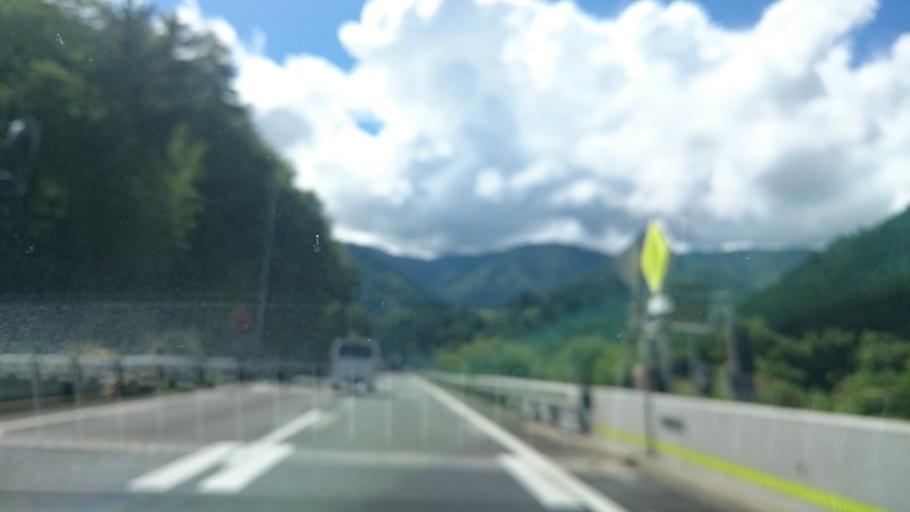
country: JP
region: Nagano
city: Iida
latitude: 35.4573
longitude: 137.6798
